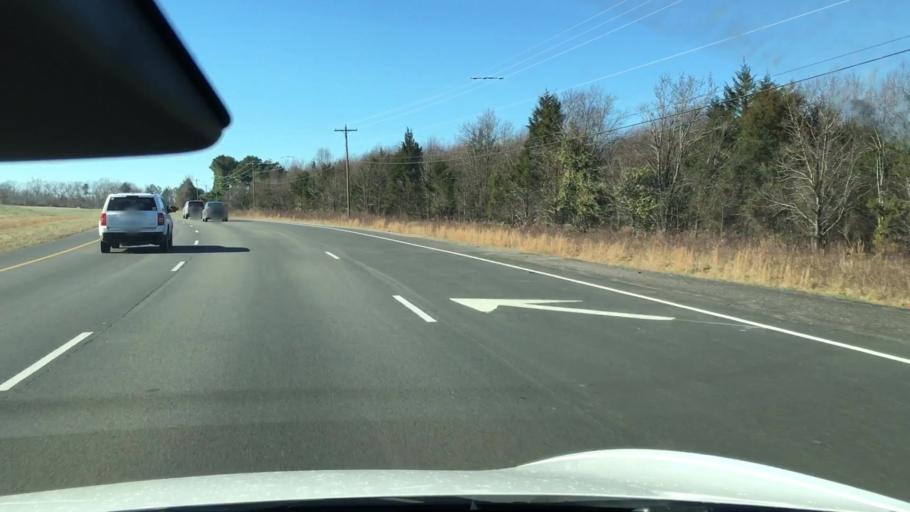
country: US
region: Virginia
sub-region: Chesterfield County
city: Woodlake
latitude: 37.5086
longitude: -77.6998
